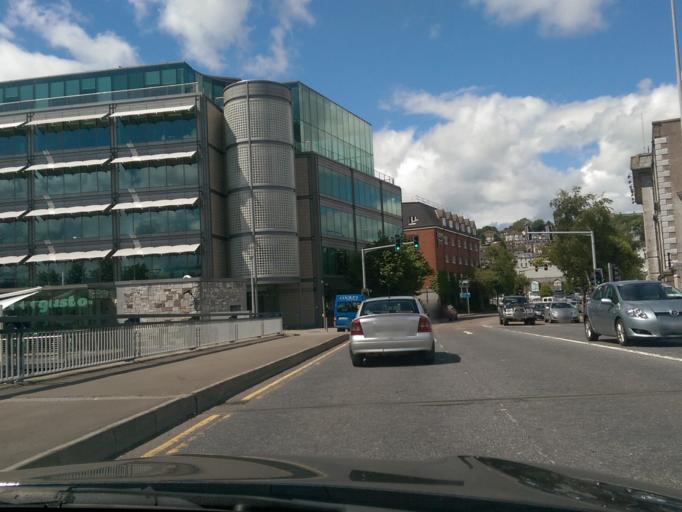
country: IE
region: Munster
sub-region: County Cork
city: Cork
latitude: 51.8984
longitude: -8.4635
